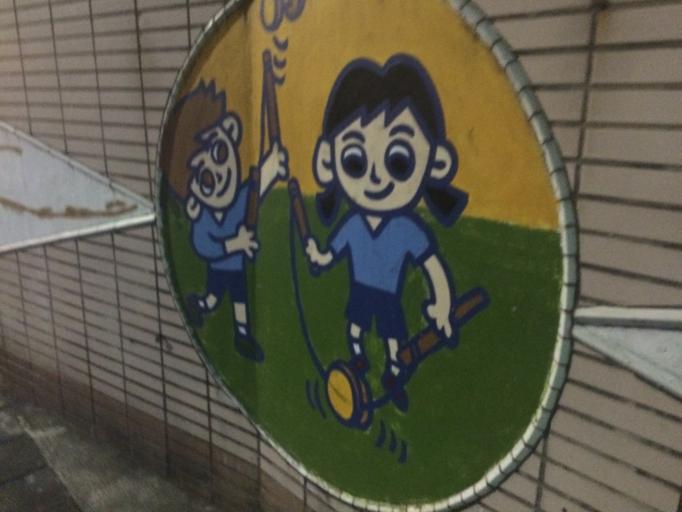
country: TW
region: Taipei
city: Taipei
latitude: 25.0265
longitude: 121.5034
